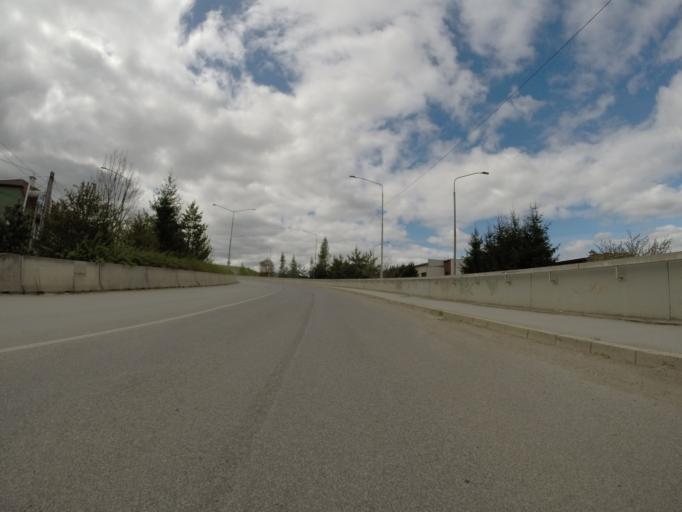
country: SK
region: Banskobystricky
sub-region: Okres Banska Bystrica
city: Brezno
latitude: 48.8003
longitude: 19.6397
